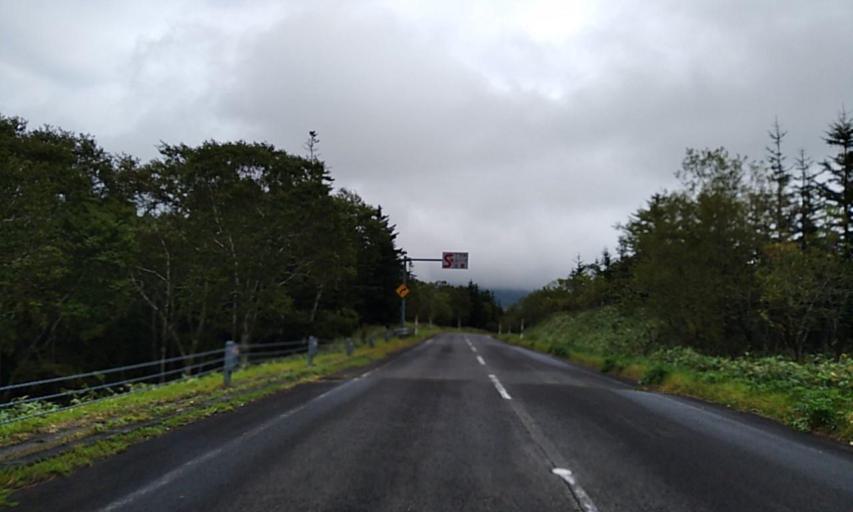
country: JP
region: Hokkaido
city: Abashiri
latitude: 43.6042
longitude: 144.5820
